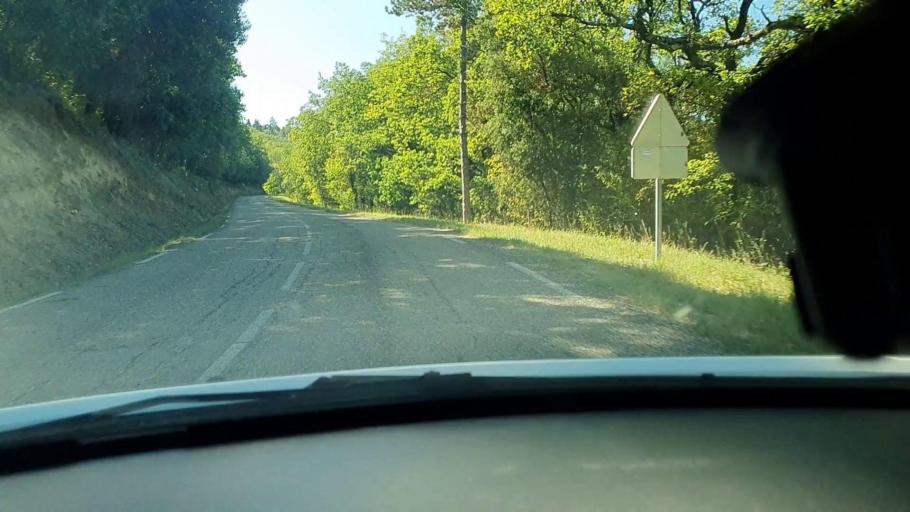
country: FR
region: Languedoc-Roussillon
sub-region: Departement du Gard
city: Saint-Paulet-de-Caisson
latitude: 44.2399
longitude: 4.5623
